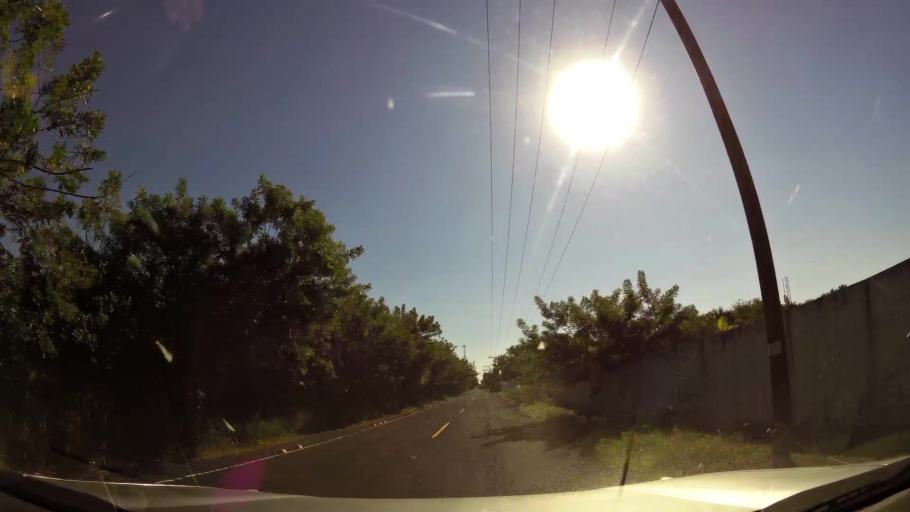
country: GT
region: Santa Rosa
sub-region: Municipio de Taxisco
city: Taxisco
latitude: 13.8878
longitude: -90.4703
